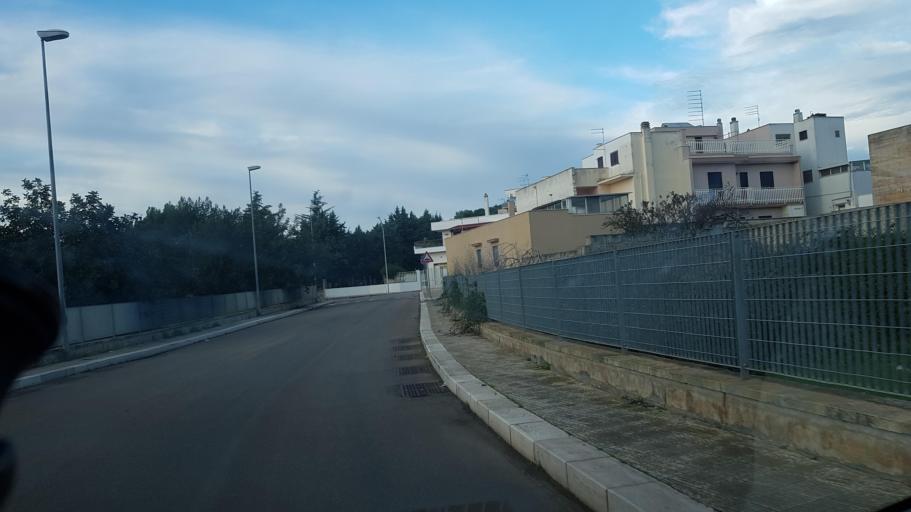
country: IT
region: Apulia
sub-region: Provincia di Brindisi
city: San Vito dei Normanni
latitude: 40.6594
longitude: 17.6994
